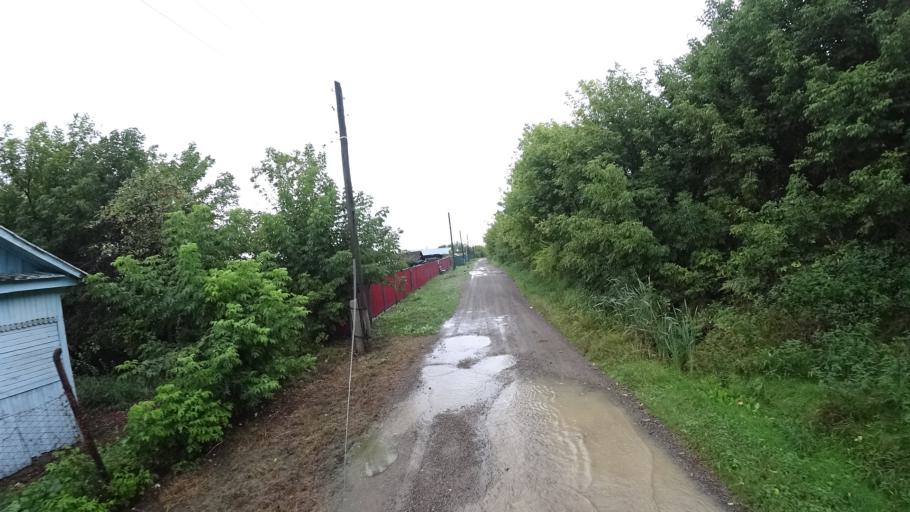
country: RU
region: Primorskiy
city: Monastyrishche
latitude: 44.2638
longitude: 132.4045
